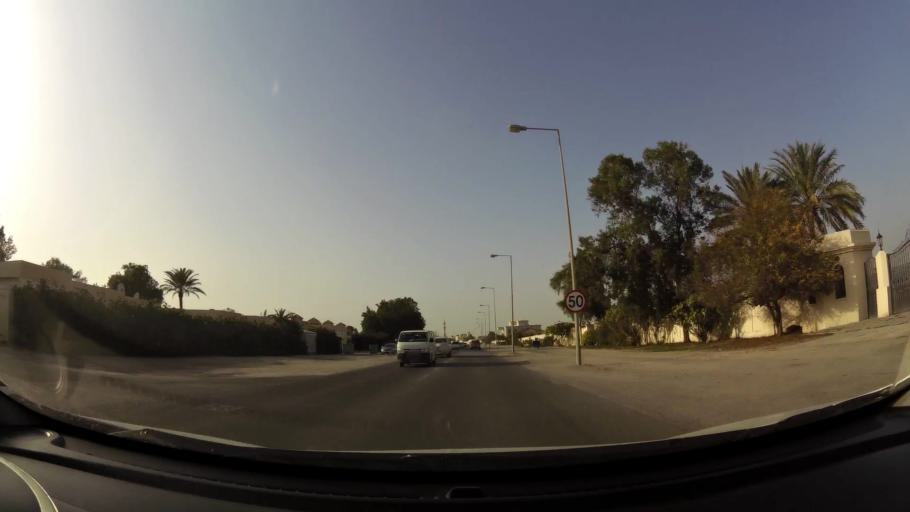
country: BH
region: Manama
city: Jidd Hafs
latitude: 26.2064
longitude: 50.4828
